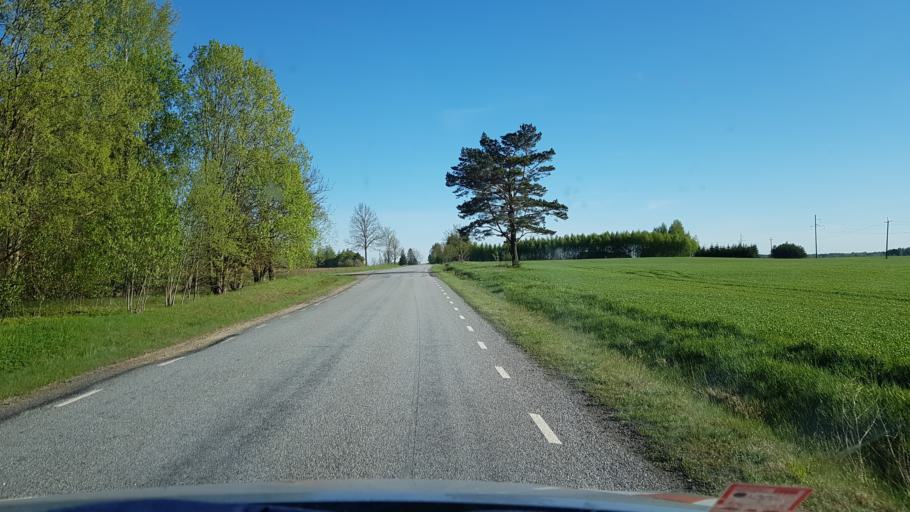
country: EE
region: Vorumaa
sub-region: Voru linn
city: Voru
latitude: 57.9309
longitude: 26.9517
